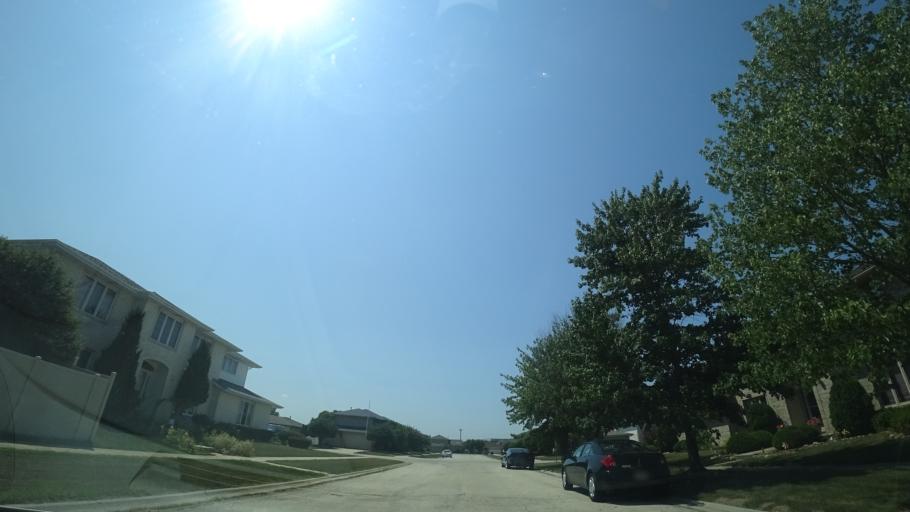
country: US
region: Illinois
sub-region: Cook County
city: Oak Lawn
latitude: 41.6959
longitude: -87.7544
